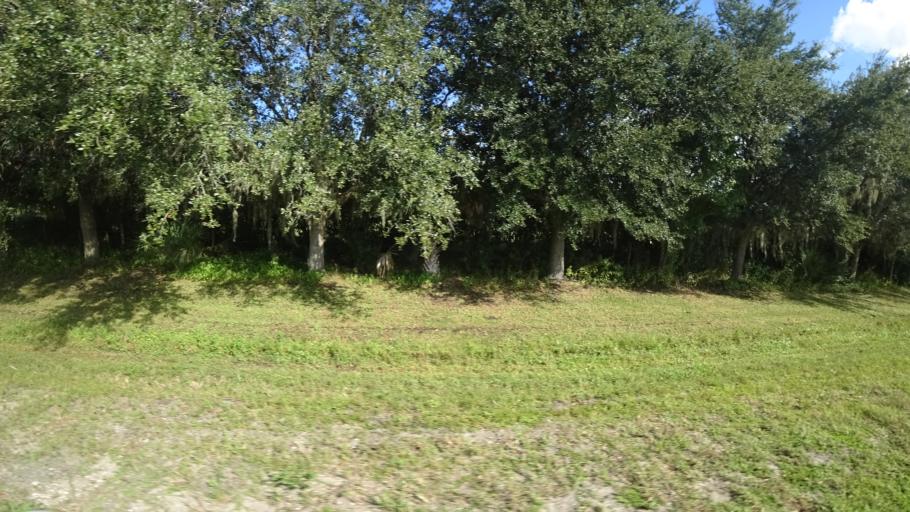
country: US
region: Florida
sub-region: Hardee County
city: Wauchula
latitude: 27.4803
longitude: -82.0797
